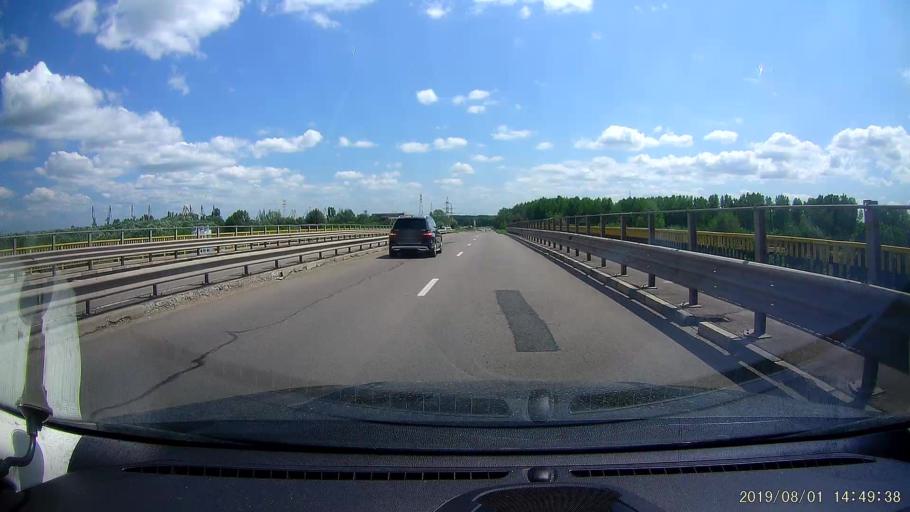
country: RO
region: Galati
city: Galati
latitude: 45.4009
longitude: 28.0154
